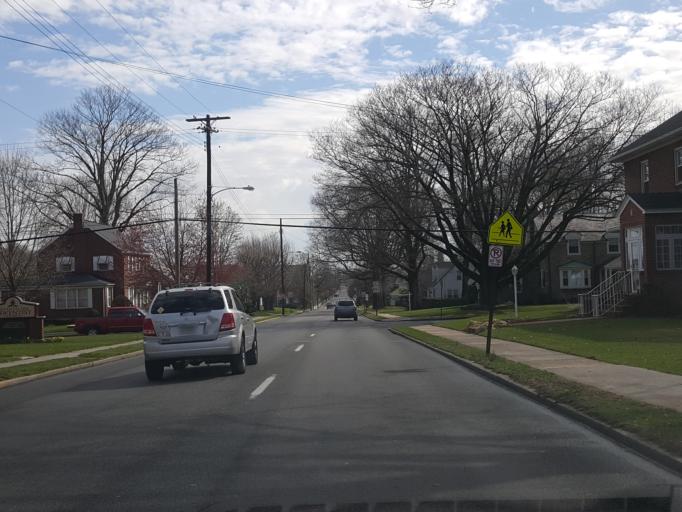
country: US
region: Pennsylvania
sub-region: Lebanon County
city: Lebanon
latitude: 40.3381
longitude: -76.4072
